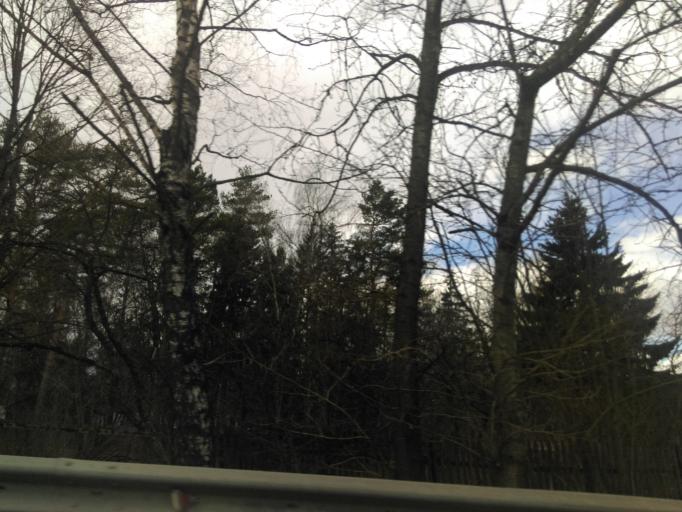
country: RU
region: Moskovskaya
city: Dorokhovo
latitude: 55.6409
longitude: 36.3270
